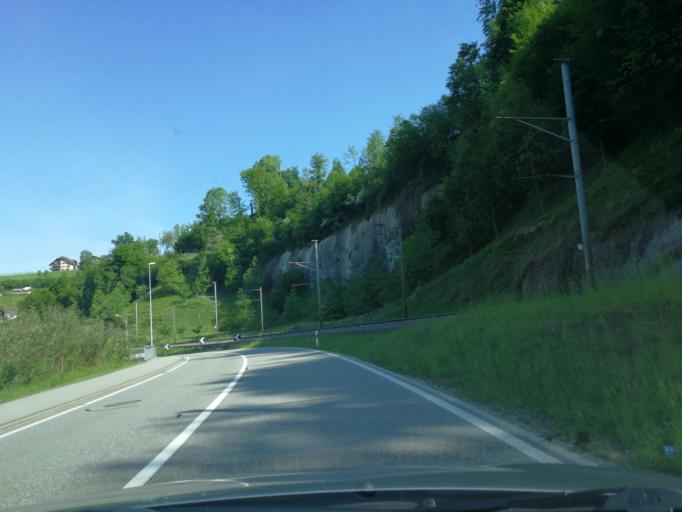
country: CH
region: Lucerne
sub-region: Entlebuch District
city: Werthenstein
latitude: 47.0556
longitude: 8.1045
